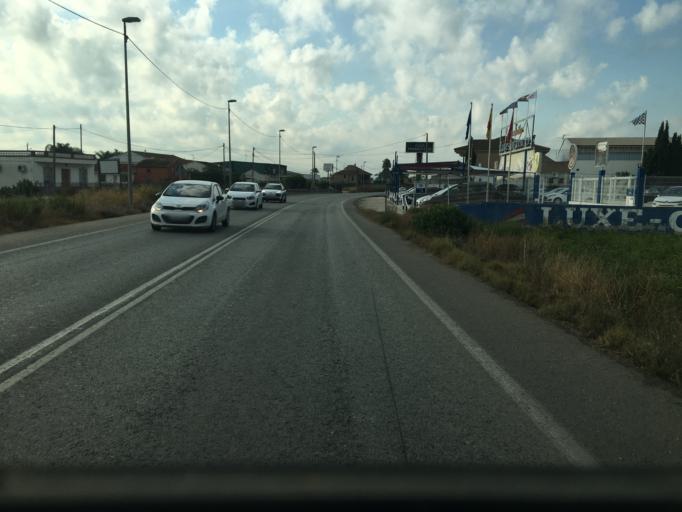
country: ES
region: Murcia
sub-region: Murcia
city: Santomera
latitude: 38.0389
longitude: -1.0470
